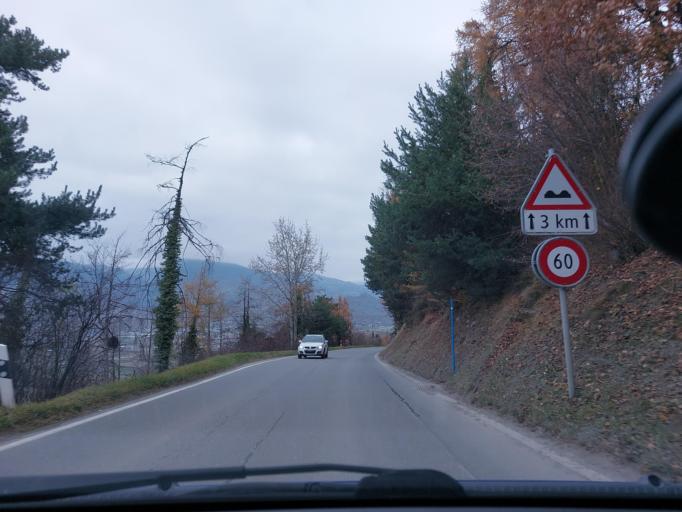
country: CH
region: Valais
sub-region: Conthey District
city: Ardon
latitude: 46.1939
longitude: 7.2823
